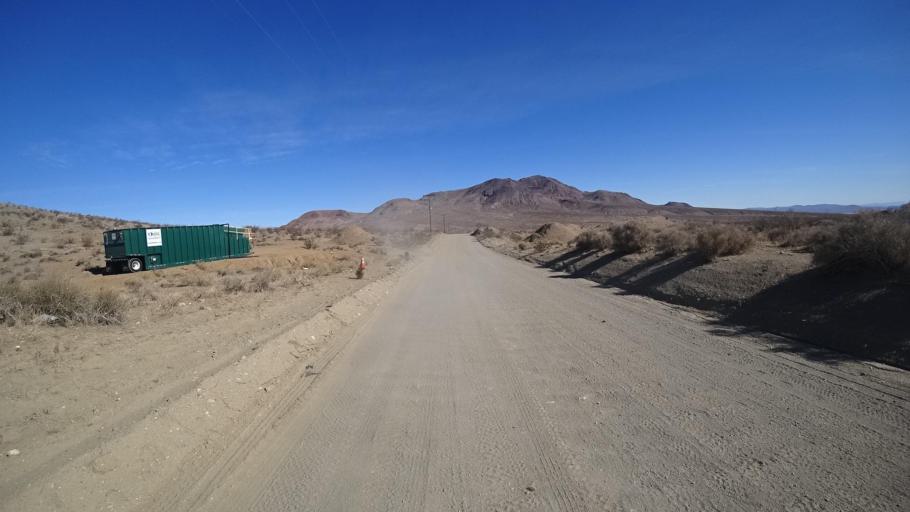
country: US
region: California
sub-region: Kern County
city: Ridgecrest
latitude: 35.3447
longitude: -117.6300
